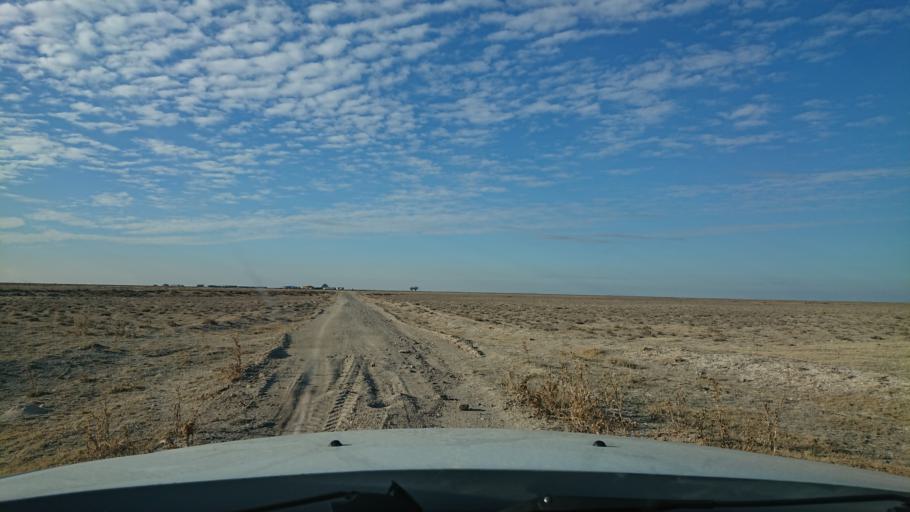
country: TR
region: Aksaray
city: Eskil
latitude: 38.5631
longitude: 33.3055
